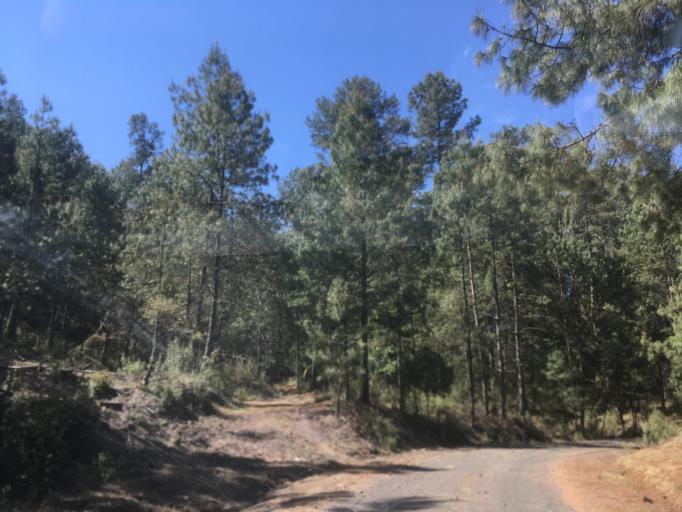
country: MX
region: Michoacan
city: Angahuan
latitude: 19.4894
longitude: -102.2038
